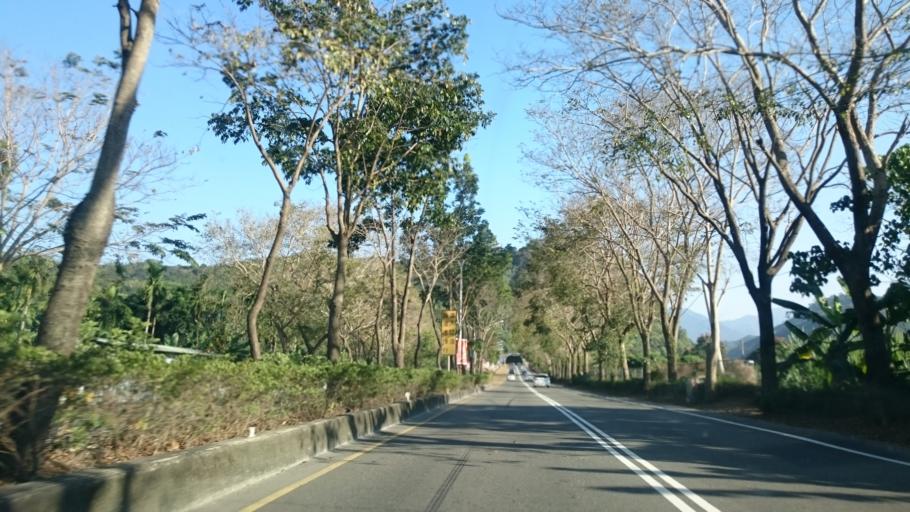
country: TW
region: Taiwan
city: Lugu
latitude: 23.8259
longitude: 120.7561
